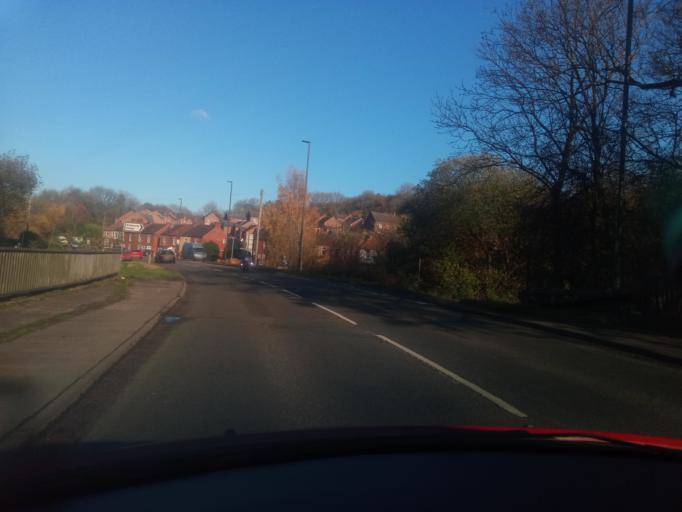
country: GB
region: England
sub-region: Derbyshire
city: Heage
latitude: 53.0621
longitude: -1.4689
